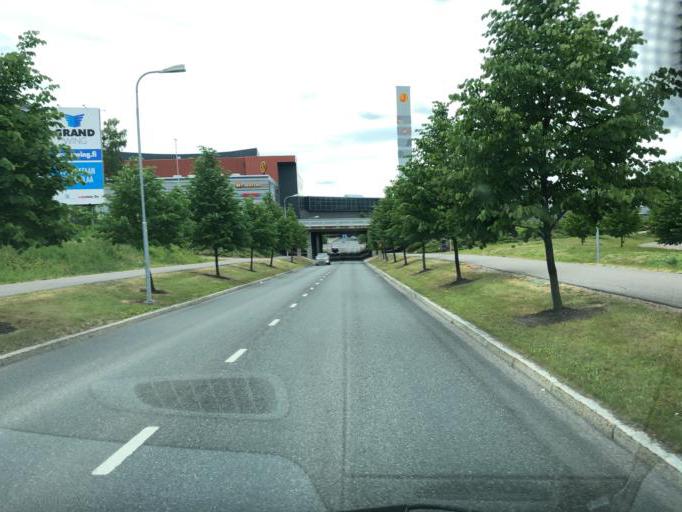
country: FI
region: Uusimaa
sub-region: Helsinki
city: Vantaa
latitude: 60.2929
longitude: 24.9711
